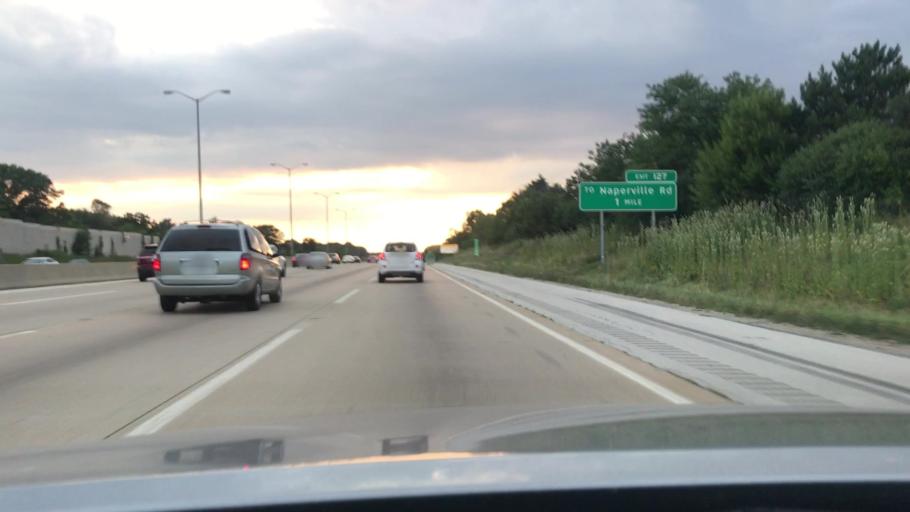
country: US
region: Illinois
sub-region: DuPage County
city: Lisle
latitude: 41.8061
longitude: -88.0975
